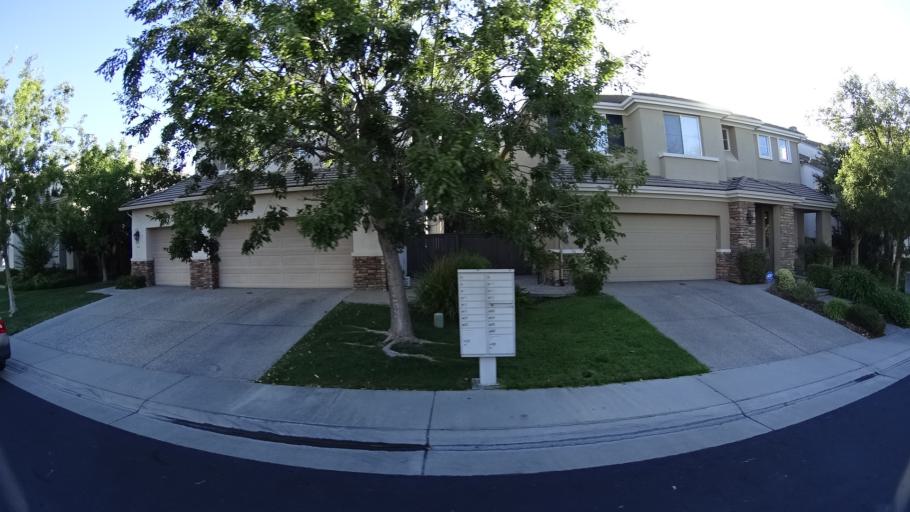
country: US
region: California
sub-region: Sacramento County
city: Laguna
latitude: 38.4020
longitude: -121.4765
